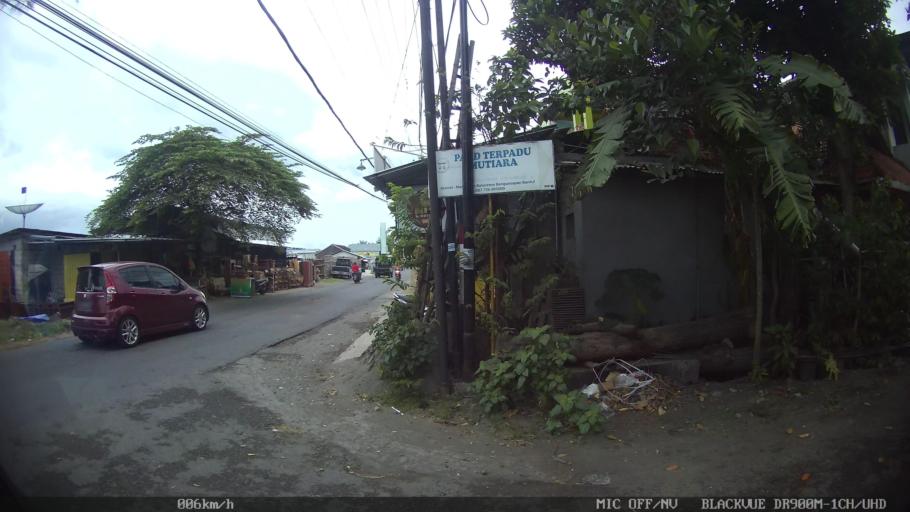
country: ID
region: Daerah Istimewa Yogyakarta
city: Sewon
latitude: -7.8338
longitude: 110.4121
